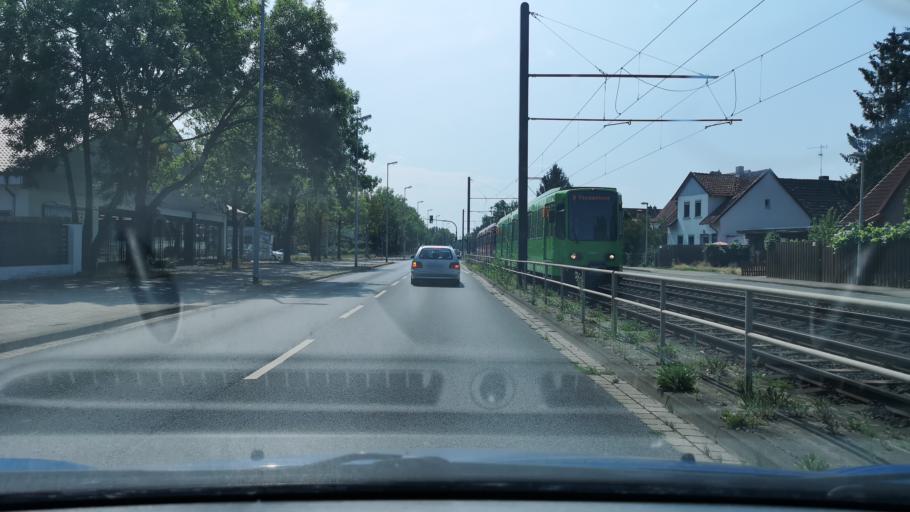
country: DE
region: Lower Saxony
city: Isernhagen Farster Bauerschaft
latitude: 52.4301
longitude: 9.8012
